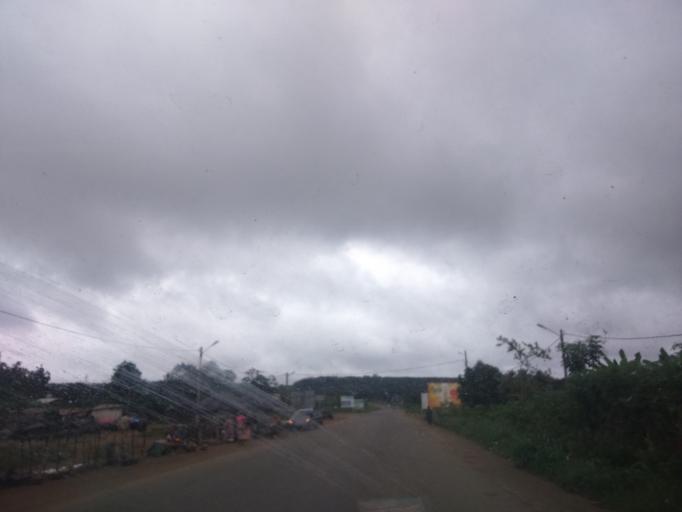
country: CI
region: Sud-Comoe
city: Bonoua
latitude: 5.2783
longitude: -3.5102
